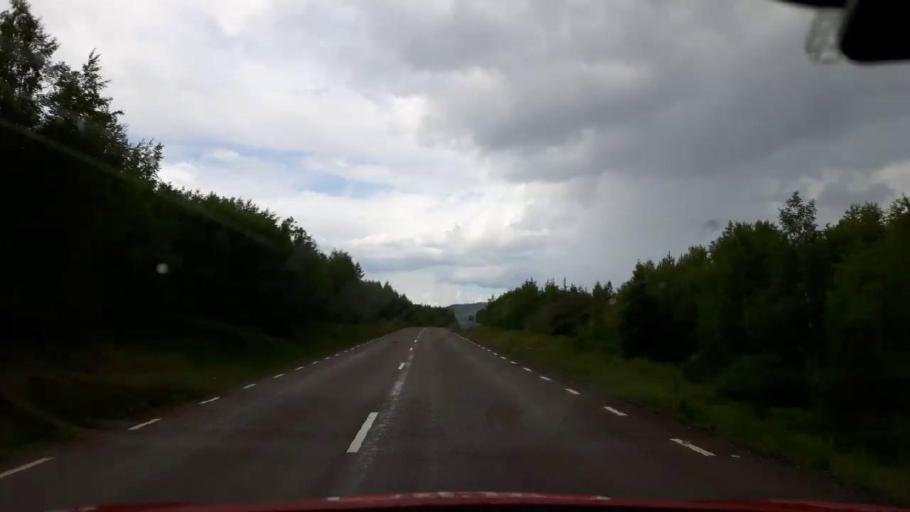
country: SE
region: Jaemtland
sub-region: Krokoms Kommun
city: Valla
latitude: 63.8910
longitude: 14.2687
